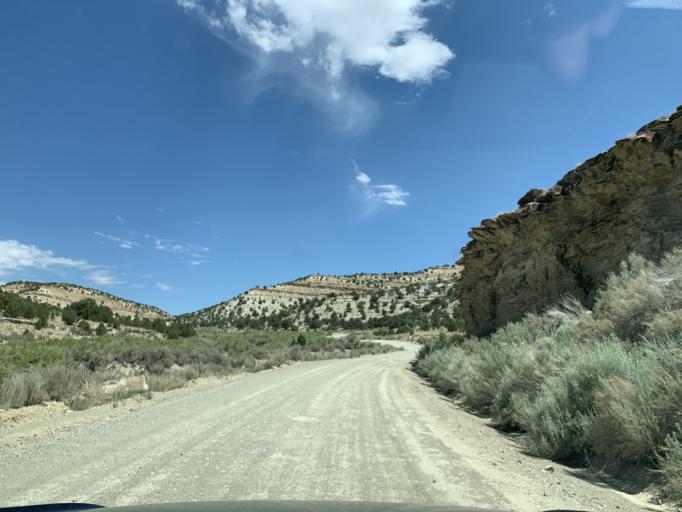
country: US
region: Utah
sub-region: Duchesne County
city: Duchesne
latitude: 39.8610
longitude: -110.2513
